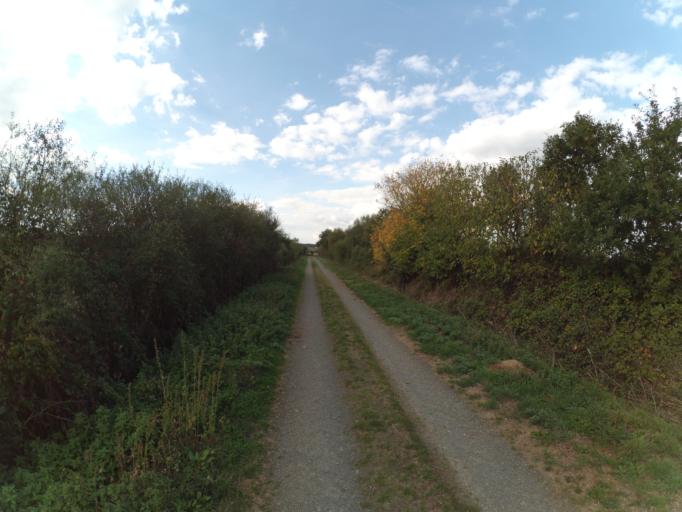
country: FR
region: Pays de la Loire
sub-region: Departement de la Loire-Atlantique
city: Saint-Lumine-de-Clisson
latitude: 47.0723
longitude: -1.3298
